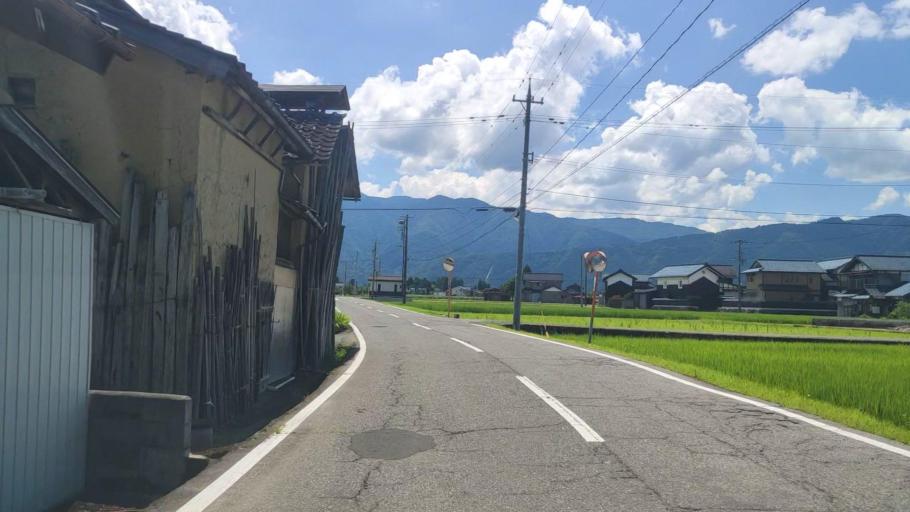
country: JP
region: Fukui
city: Ono
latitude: 35.9606
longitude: 136.5323
